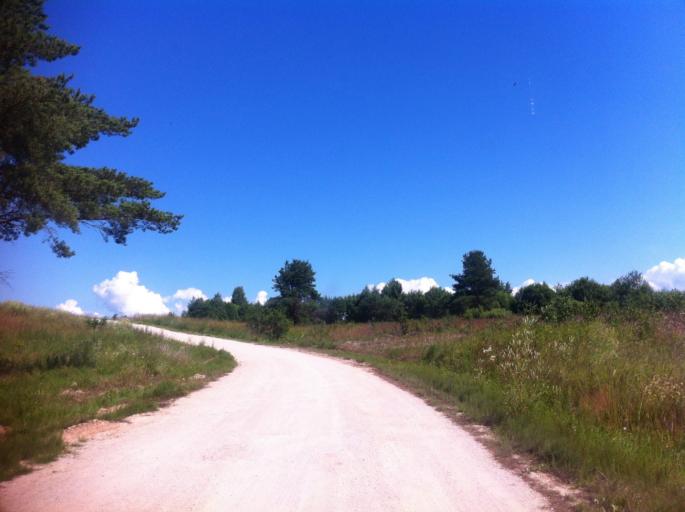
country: RU
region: Pskov
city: Izborsk
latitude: 57.8230
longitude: 27.9657
